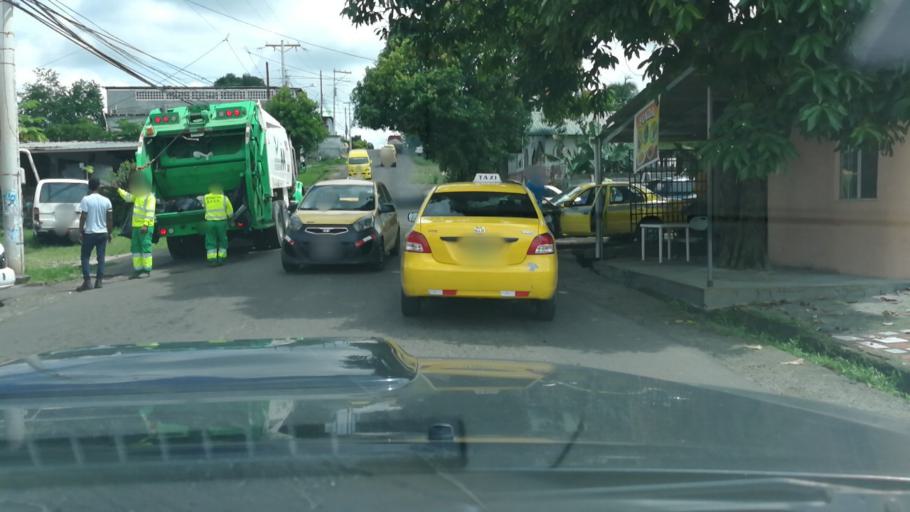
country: PA
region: Panama
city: Tocumen
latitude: 9.0970
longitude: -79.4097
